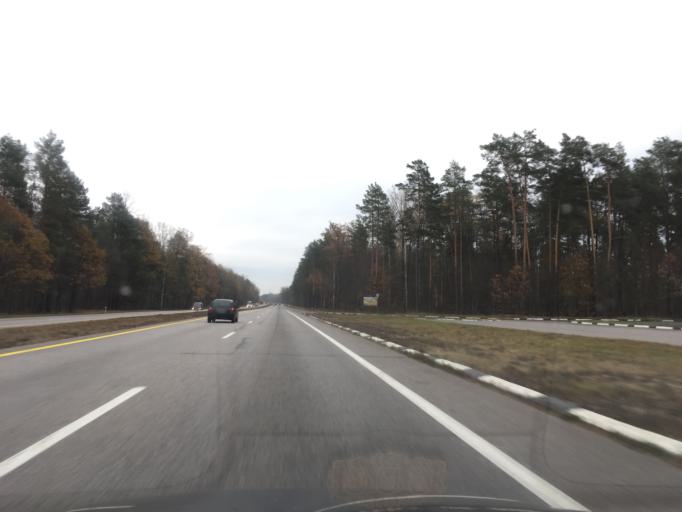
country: BY
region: Gomel
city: Kastsyukowka
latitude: 52.3582
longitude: 30.7121
